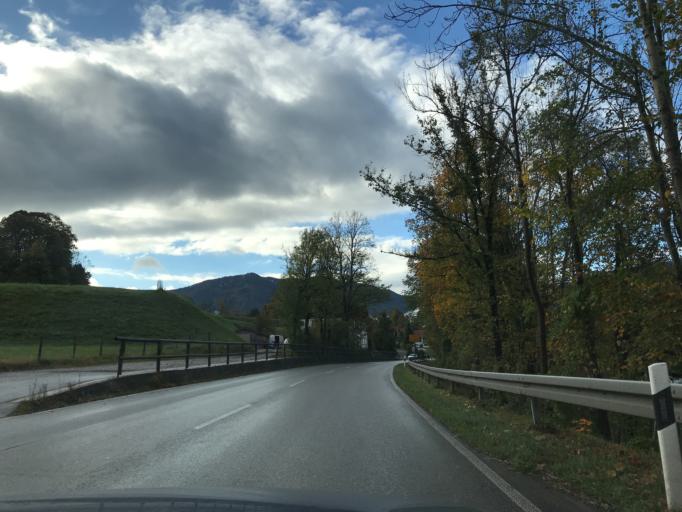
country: DE
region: Bavaria
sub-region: Upper Bavaria
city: Lenggries
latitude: 47.6561
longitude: 11.5890
